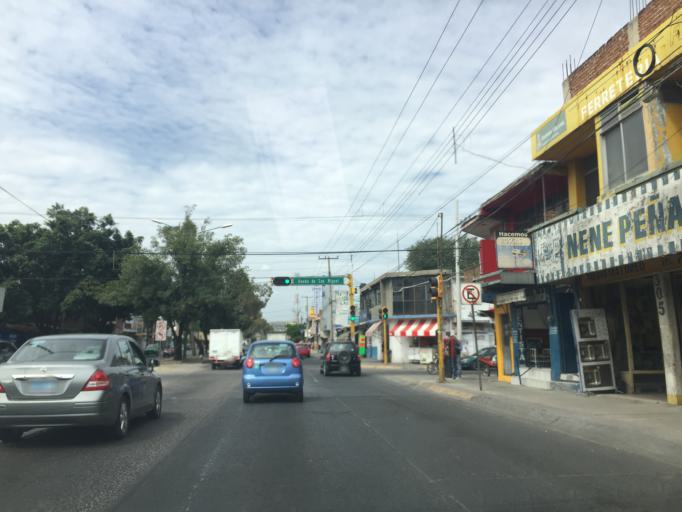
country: MX
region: Guanajuato
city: Leon
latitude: 21.1022
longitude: -101.6853
